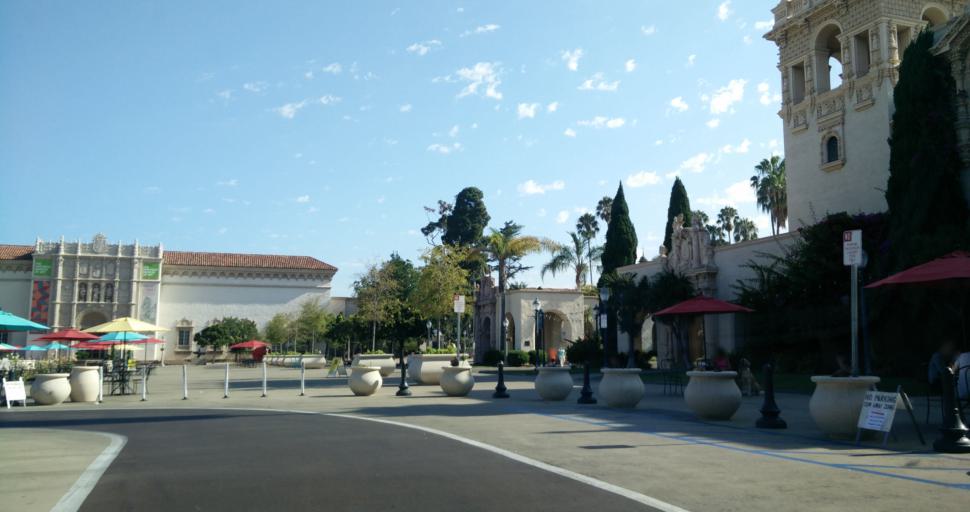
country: US
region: California
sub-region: San Diego County
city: San Diego
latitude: 32.7310
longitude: -117.1503
